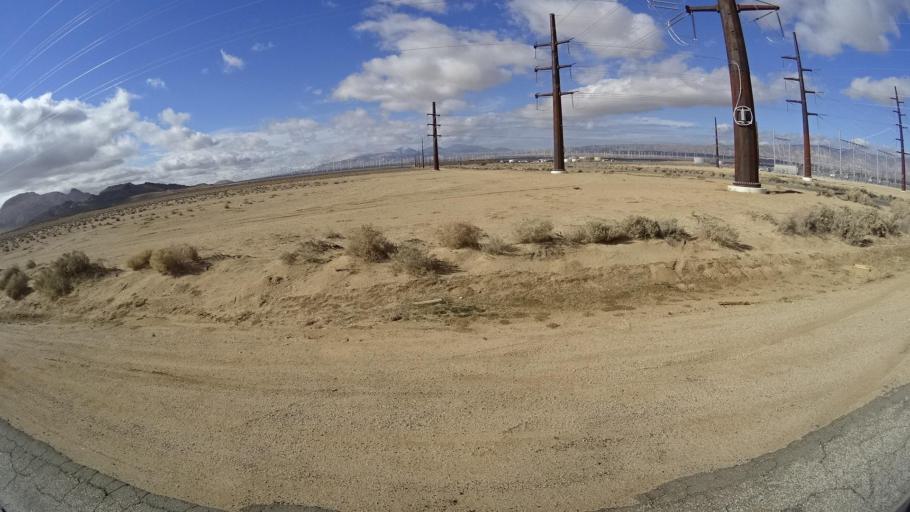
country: US
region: California
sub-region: Kern County
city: Mojave
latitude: 35.0248
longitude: -118.1497
